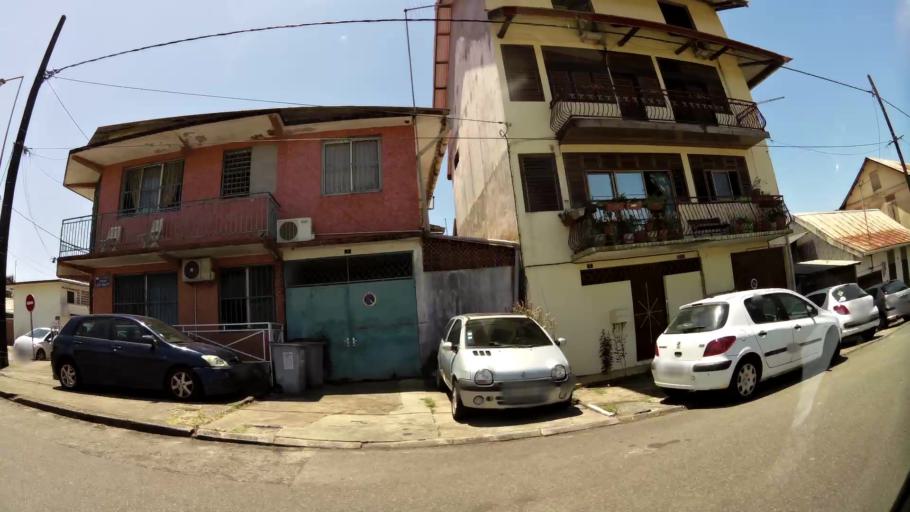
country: GF
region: Guyane
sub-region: Guyane
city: Cayenne
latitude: 4.9309
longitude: -52.3321
